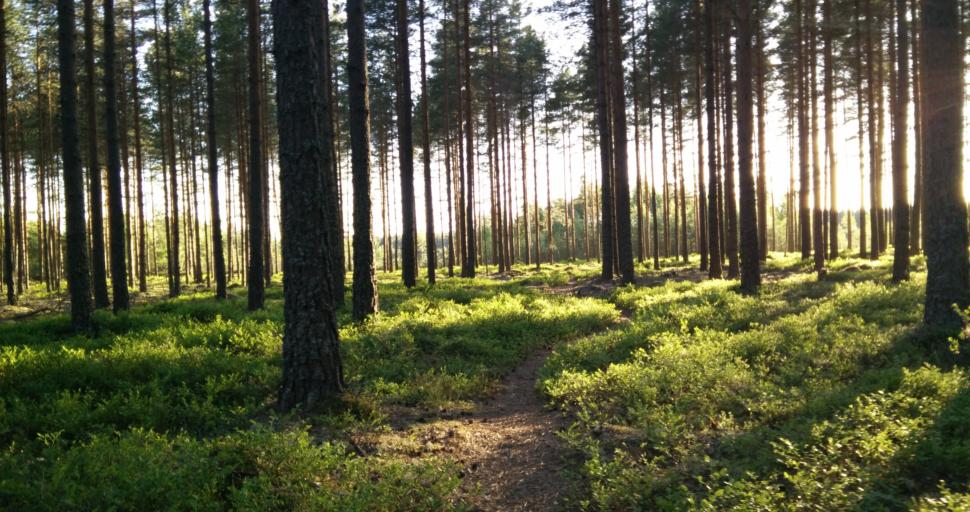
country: SE
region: Vaermland
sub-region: Hagfors Kommun
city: Hagfors
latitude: 60.0173
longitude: 13.5848
